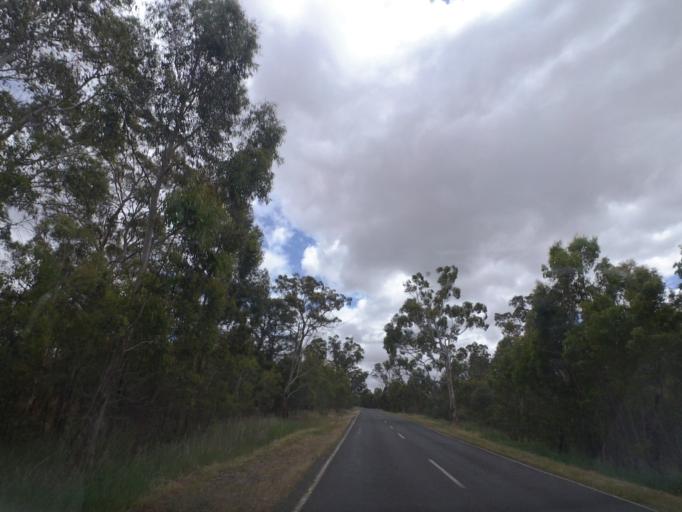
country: AU
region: Victoria
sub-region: Whittlesea
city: Whittlesea
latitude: -37.2912
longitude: 145.0577
